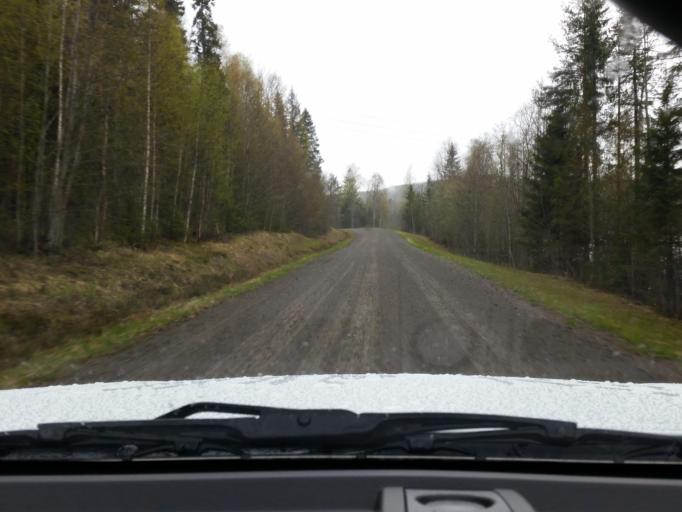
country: SE
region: Norrbotten
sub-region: Pitea Kommun
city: Norrfjarden
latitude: 65.6106
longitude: 21.4136
